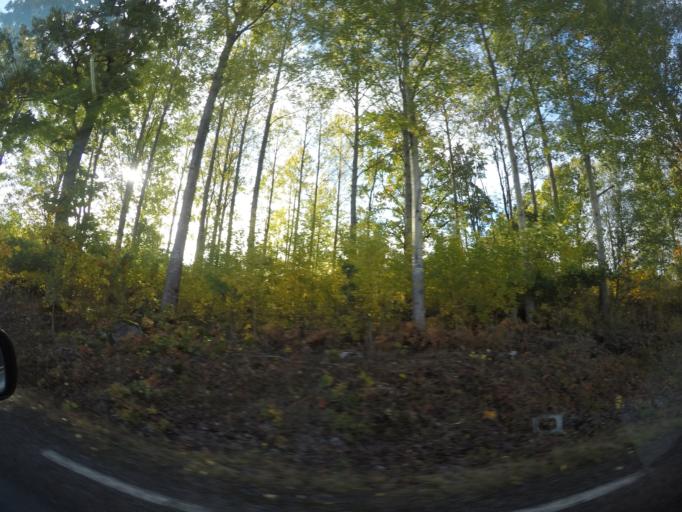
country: SE
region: Soedermanland
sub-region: Eskilstuna Kommun
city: Kvicksund
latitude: 59.3460
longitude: 16.2539
